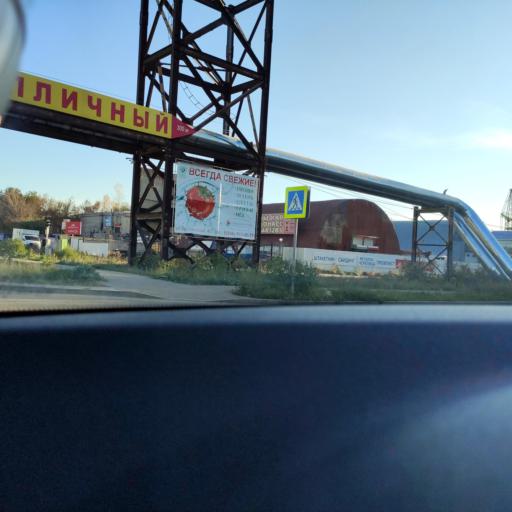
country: RU
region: Samara
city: Smyshlyayevka
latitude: 53.1919
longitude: 50.2947
